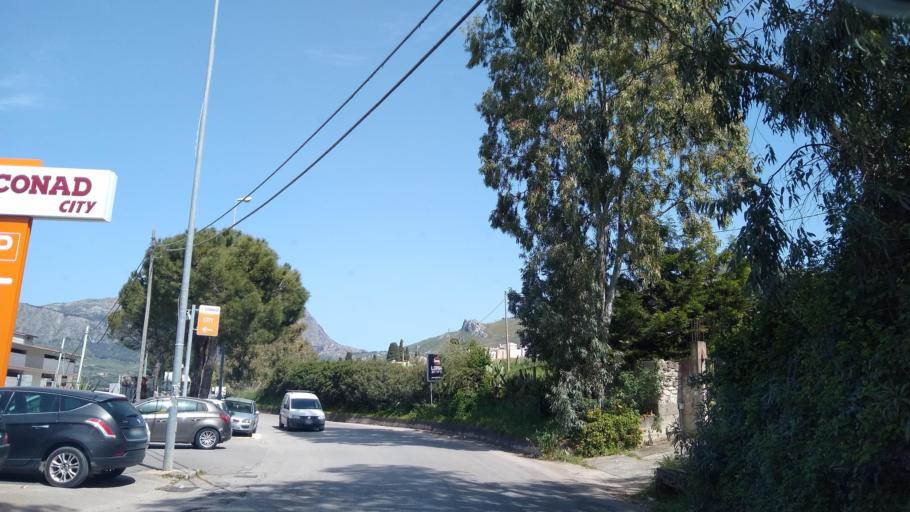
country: IT
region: Sicily
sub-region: Palermo
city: San Giuseppe Jato
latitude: 37.9752
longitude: 13.1973
